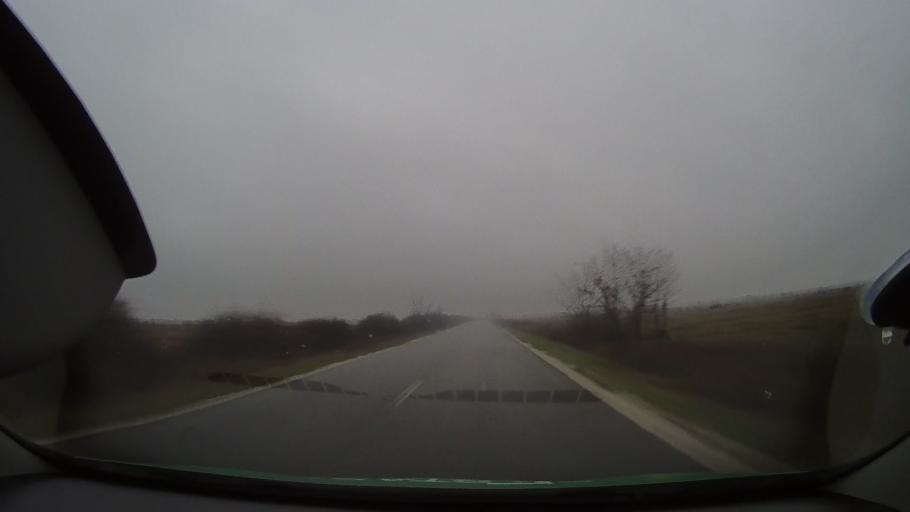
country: RO
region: Arad
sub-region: Comuna Craiova
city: Craiova
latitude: 46.6084
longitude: 21.9580
